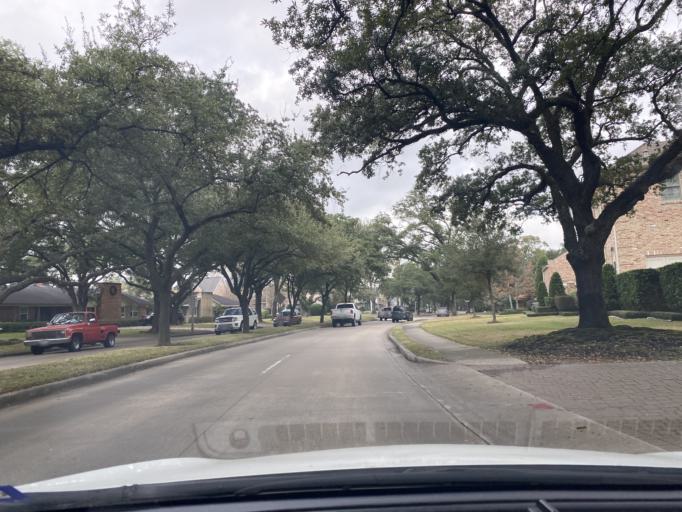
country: US
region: Texas
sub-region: Harris County
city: Hunters Creek Village
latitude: 29.7516
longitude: -95.4771
